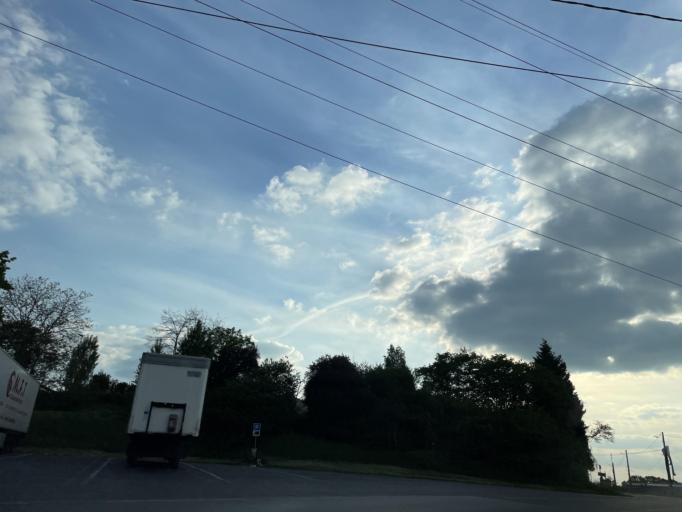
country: FR
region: Ile-de-France
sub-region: Departement de Seine-et-Marne
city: Coulommiers
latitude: 48.8086
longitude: 3.1039
